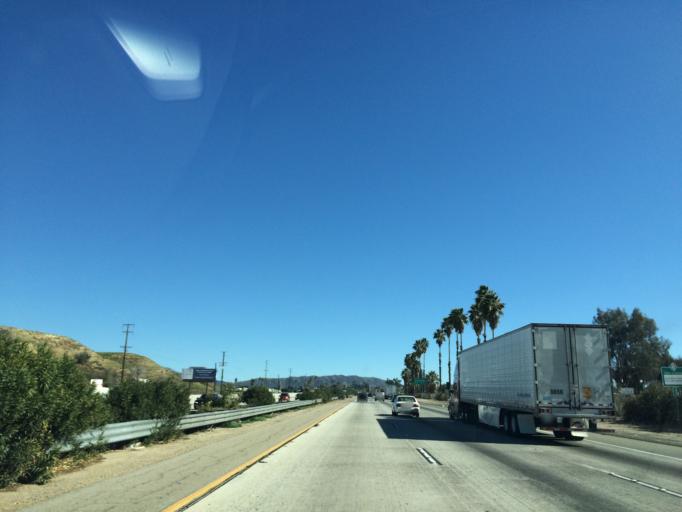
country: US
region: California
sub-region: Riverside County
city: Calimesa
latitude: 34.0137
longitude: -117.0798
